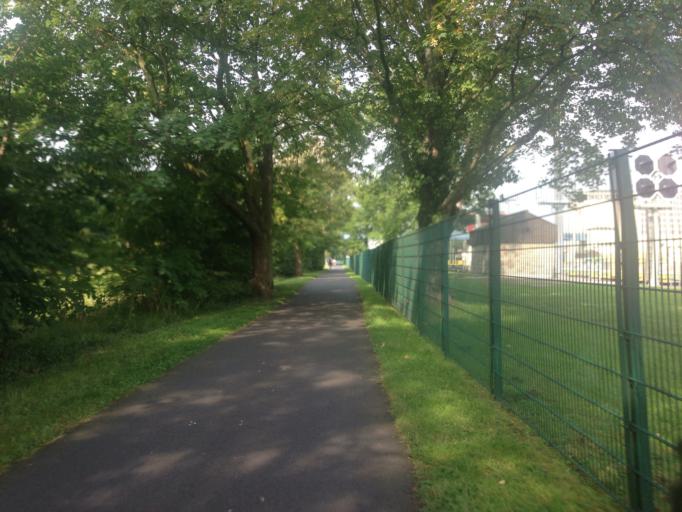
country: DE
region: Hesse
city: Niederrad
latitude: 50.0880
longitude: 8.6020
